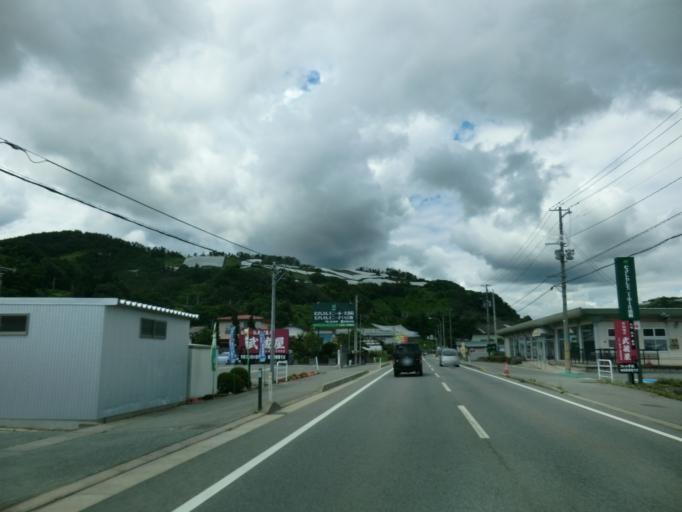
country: JP
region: Yamagata
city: Takahata
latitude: 38.0537
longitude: 140.1719
